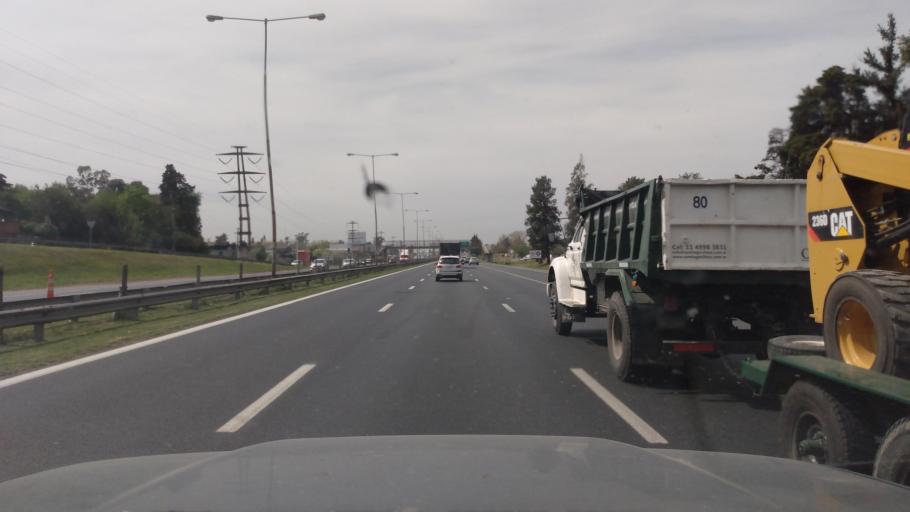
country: AR
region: Buenos Aires
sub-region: Partido de Pilar
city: Pilar
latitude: -34.4509
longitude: -58.9144
